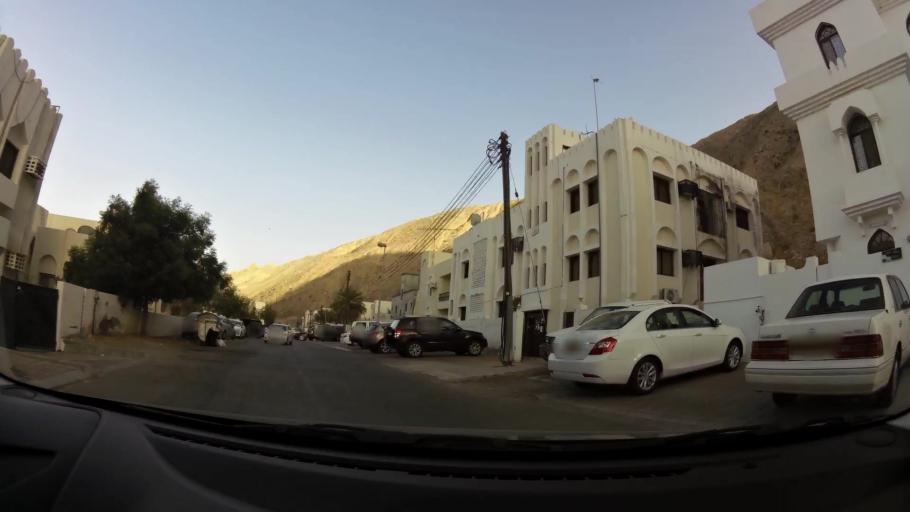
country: OM
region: Muhafazat Masqat
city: Muscat
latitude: 23.5686
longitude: 58.5687
